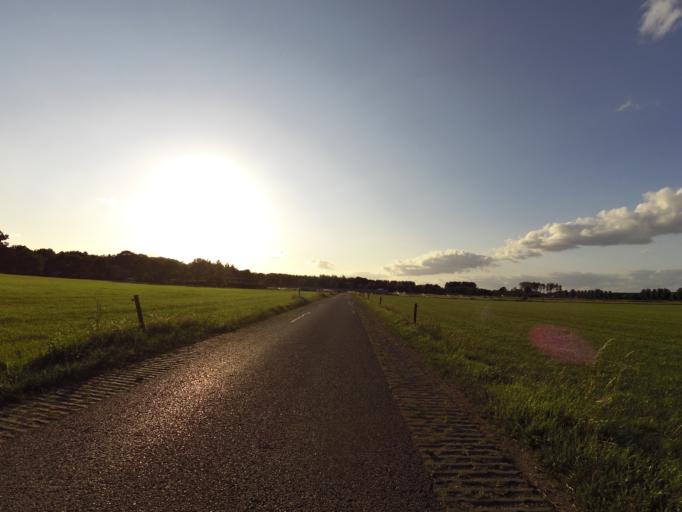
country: NL
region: Gelderland
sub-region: Gemeente Doetinchem
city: Doetinchem
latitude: 51.9874
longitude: 6.2857
